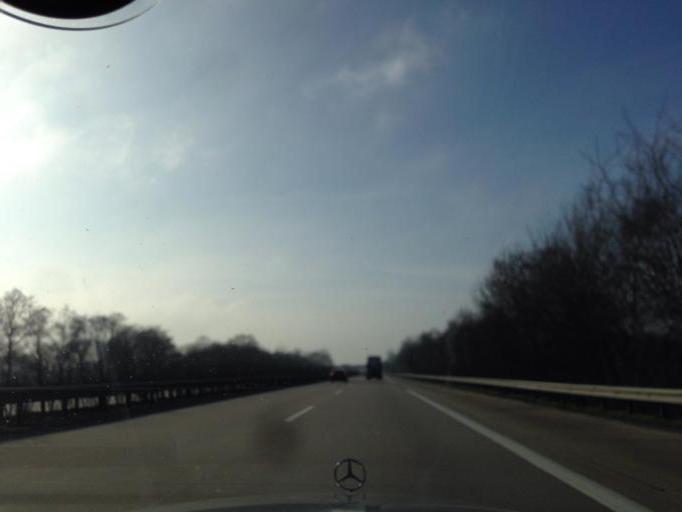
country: DE
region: Lower Saxony
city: Gross Ippener
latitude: 52.9846
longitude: 8.6392
